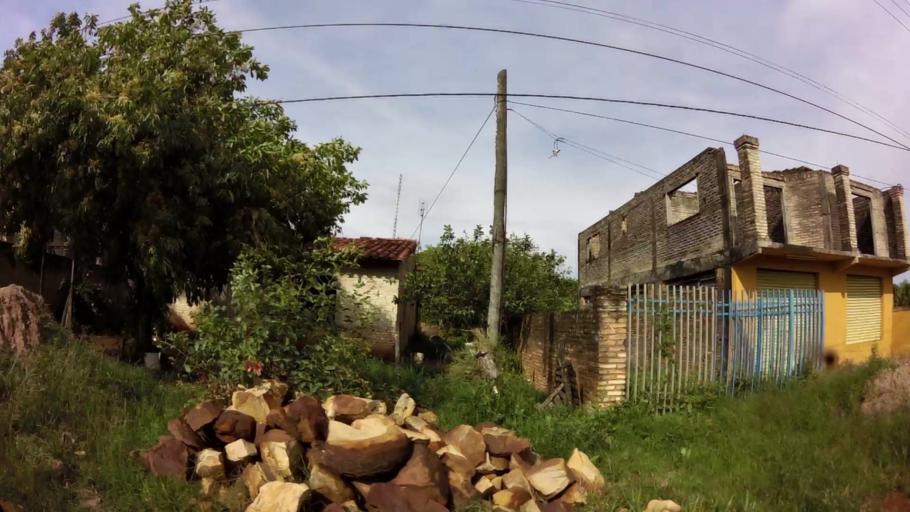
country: PY
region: Central
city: Limpio
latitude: -25.1785
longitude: -57.4954
